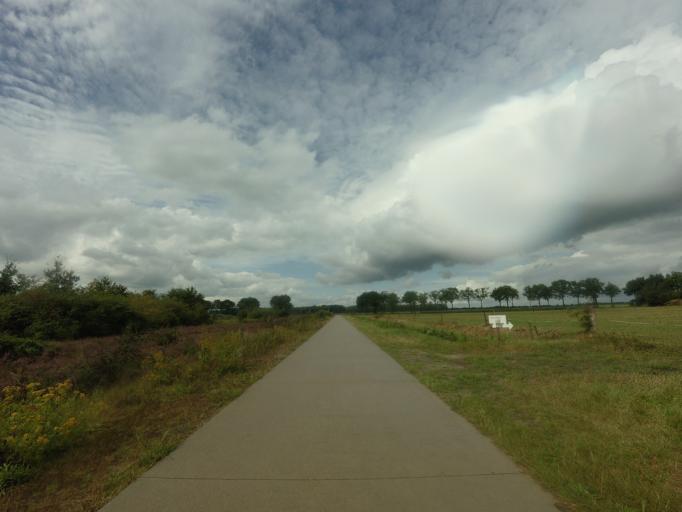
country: NL
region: Overijssel
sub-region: Gemeente Dalfsen
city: Dalfsen
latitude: 52.6108
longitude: 6.3432
